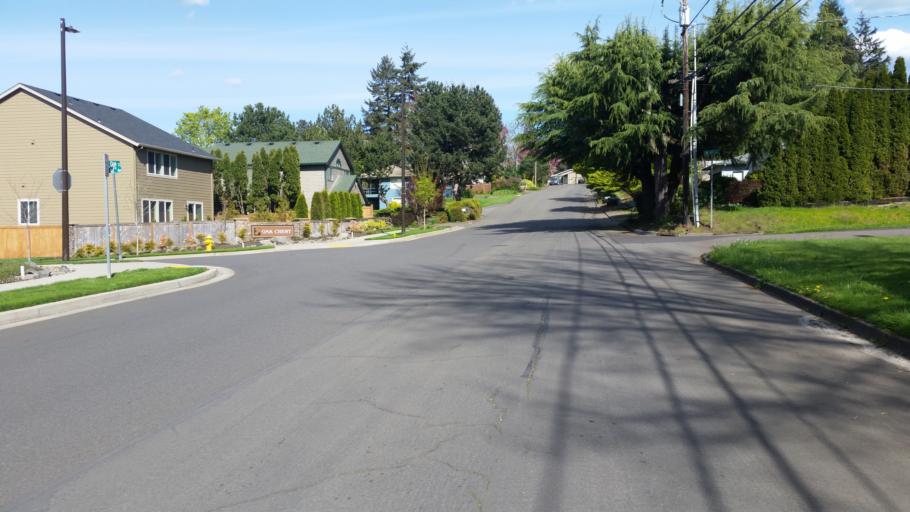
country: US
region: Oregon
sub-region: Washington County
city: Metzger
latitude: 45.4447
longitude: -122.7464
